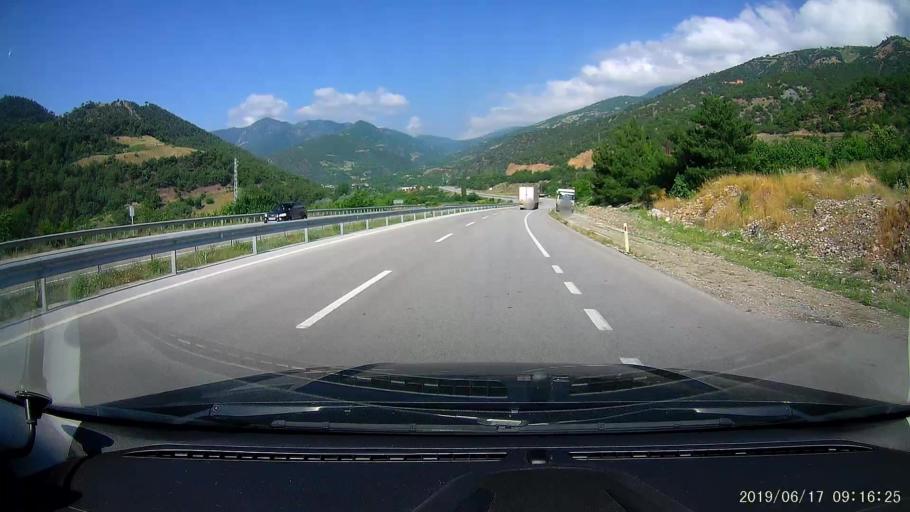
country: TR
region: Amasya
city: Akdag
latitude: 40.7444
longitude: 36.0114
